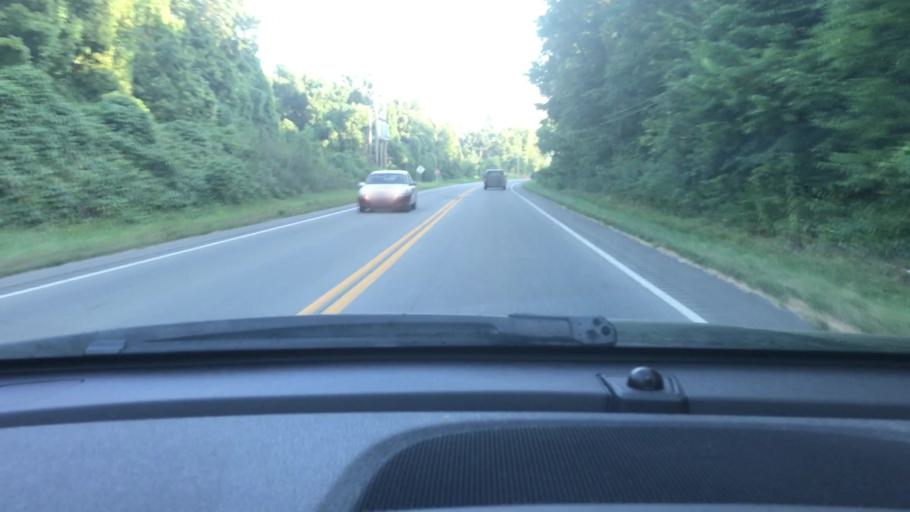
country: US
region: Tennessee
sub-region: Dickson County
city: Charlotte
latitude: 36.1539
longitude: -87.3564
